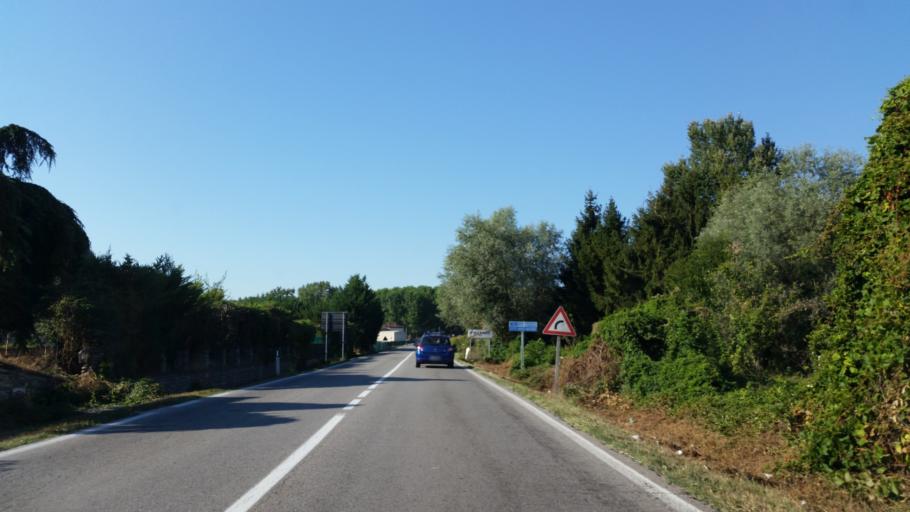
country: IT
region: Piedmont
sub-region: Provincia di Cuneo
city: Cinzano
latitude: 44.6829
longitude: 7.8918
